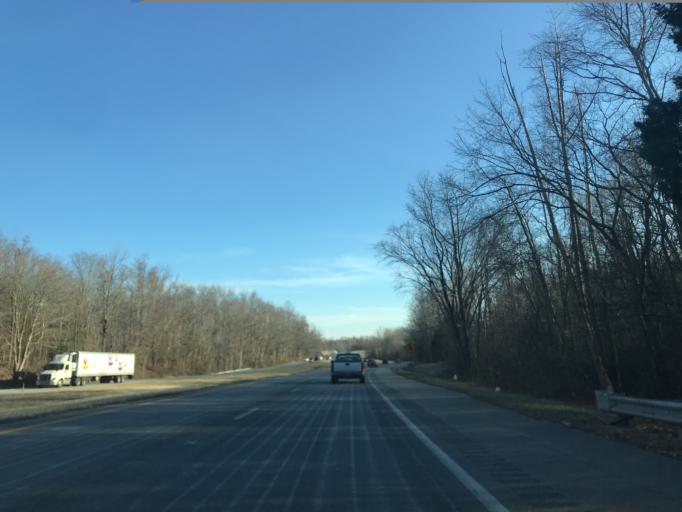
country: US
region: Maryland
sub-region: Prince George's County
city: Marlboro Meadows
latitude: 38.7899
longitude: -76.6673
